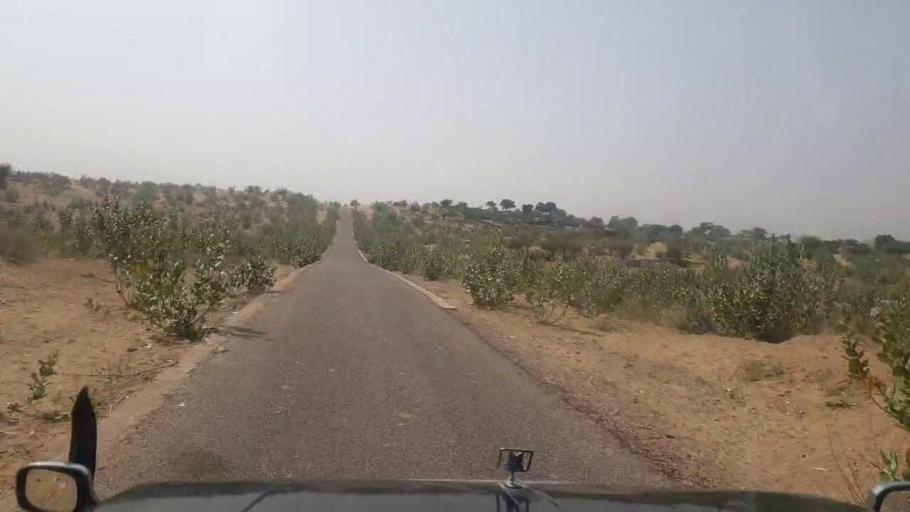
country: PK
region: Sindh
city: Islamkot
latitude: 25.0849
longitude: 70.1550
